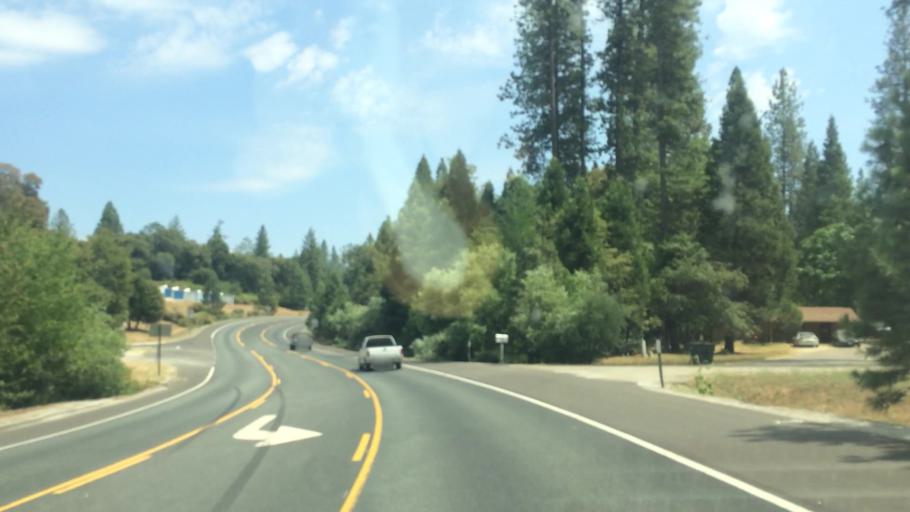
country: US
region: California
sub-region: Amador County
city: Pine Grove
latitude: 38.4075
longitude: -120.6500
